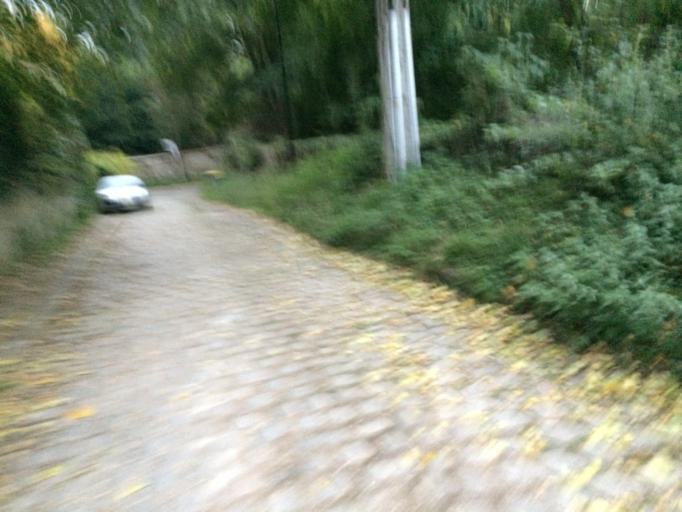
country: FR
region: Ile-de-France
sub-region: Departement des Yvelines
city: Velizy-Villacoublay
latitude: 48.7621
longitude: 2.1951
